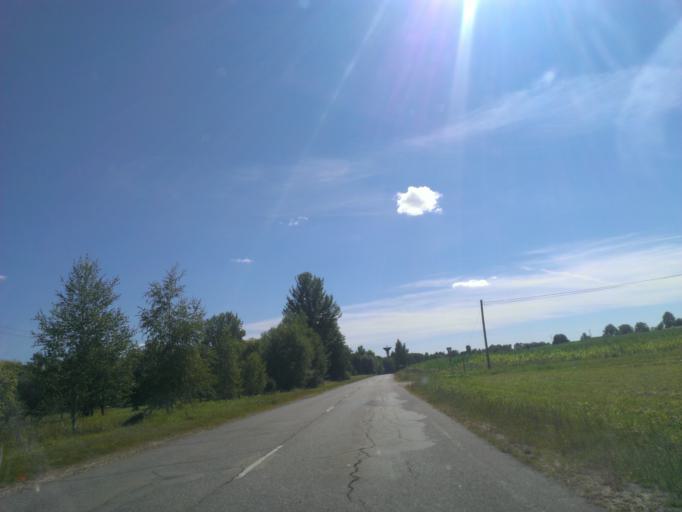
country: LV
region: Malpils
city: Malpils
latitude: 57.0168
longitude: 24.9445
